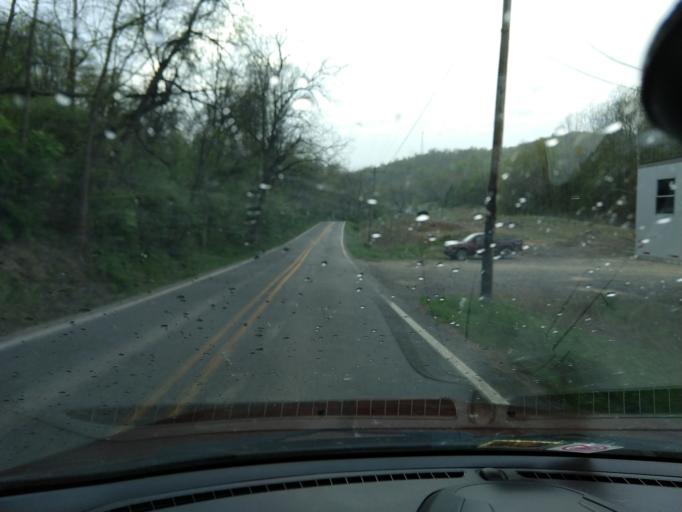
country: US
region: West Virginia
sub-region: Harrison County
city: Despard
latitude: 39.3339
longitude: -80.2848
